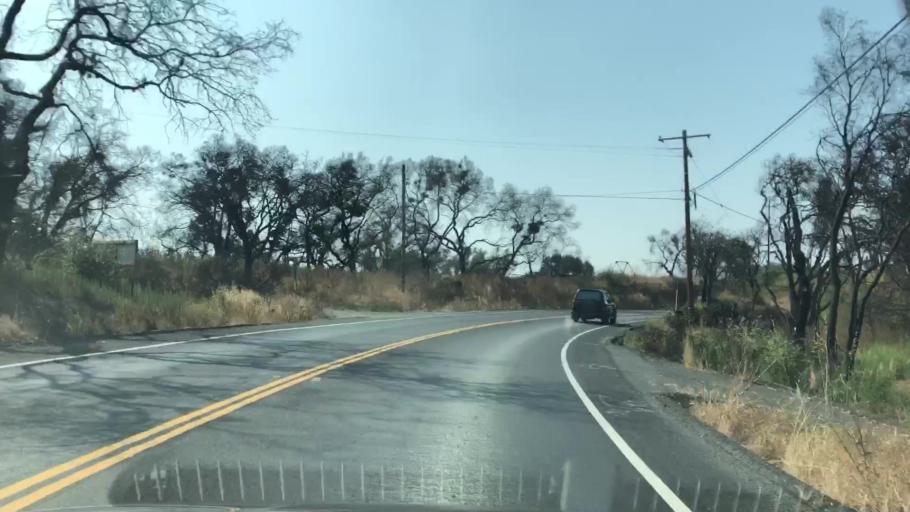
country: US
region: California
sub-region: Sonoma County
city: Larkfield-Wikiup
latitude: 38.5216
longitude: -122.7184
